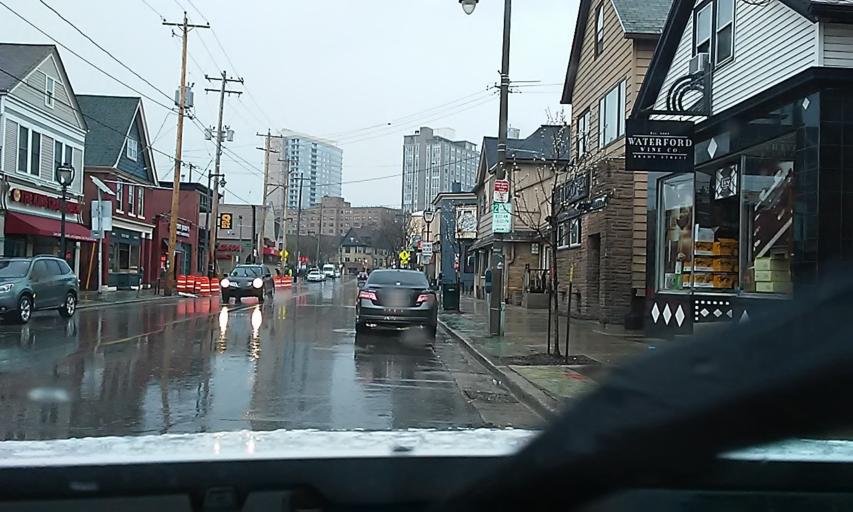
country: US
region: Wisconsin
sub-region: Milwaukee County
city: Milwaukee
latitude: 43.0530
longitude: -87.8946
